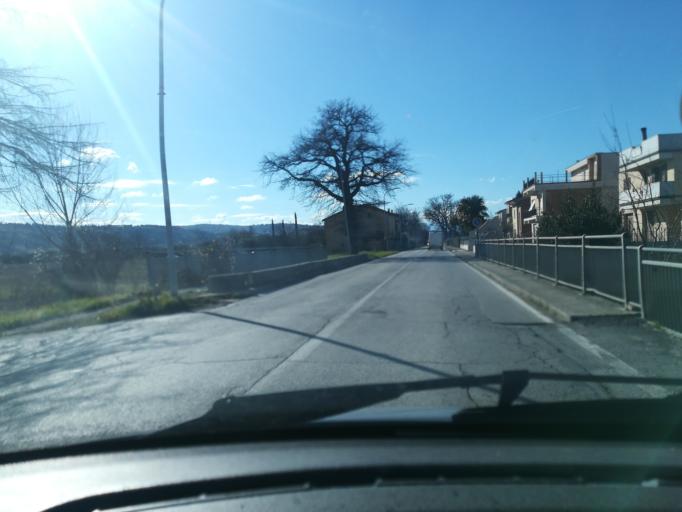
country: IT
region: The Marches
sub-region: Provincia di Macerata
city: Montecassiano
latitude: 43.3459
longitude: 13.4335
